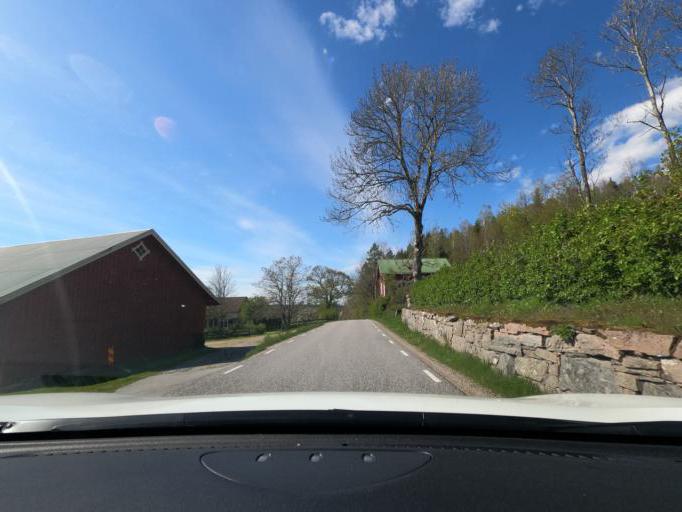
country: SE
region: Vaestra Goetaland
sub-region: Harryda Kommun
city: Ravlanda
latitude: 57.6357
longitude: 12.4984
